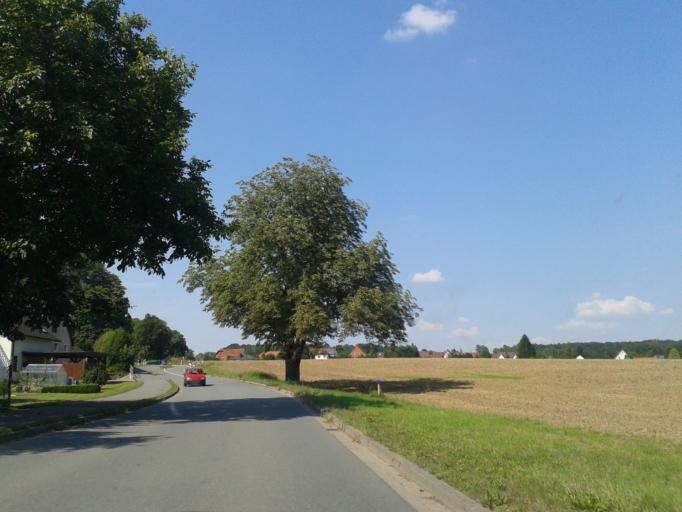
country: DE
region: North Rhine-Westphalia
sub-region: Regierungsbezirk Detmold
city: Steinheim
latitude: 51.8930
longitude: 9.0607
